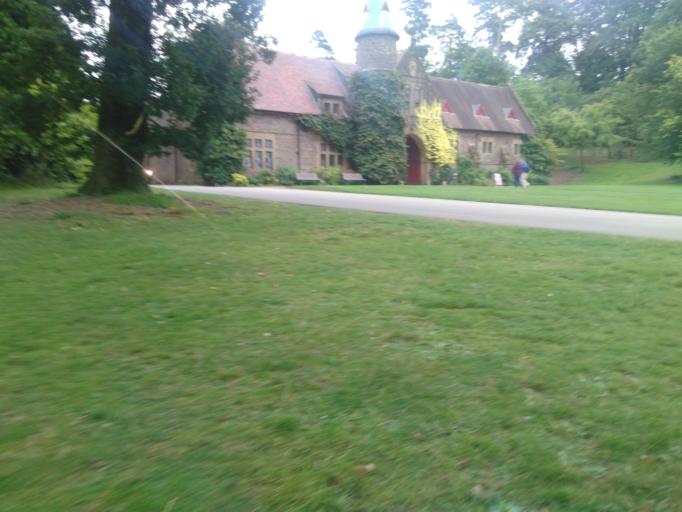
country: GB
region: England
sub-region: Devon
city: Tiverton
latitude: 50.9286
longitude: -3.4802
